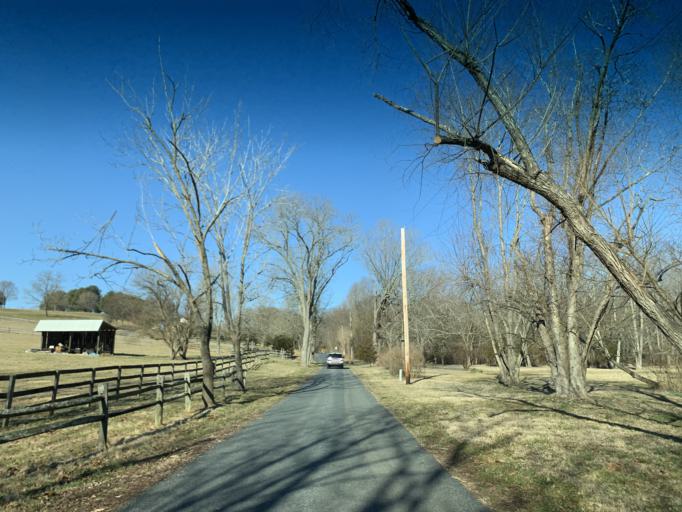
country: US
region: Maryland
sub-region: Harford County
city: South Bel Air
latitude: 39.6178
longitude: -76.2404
